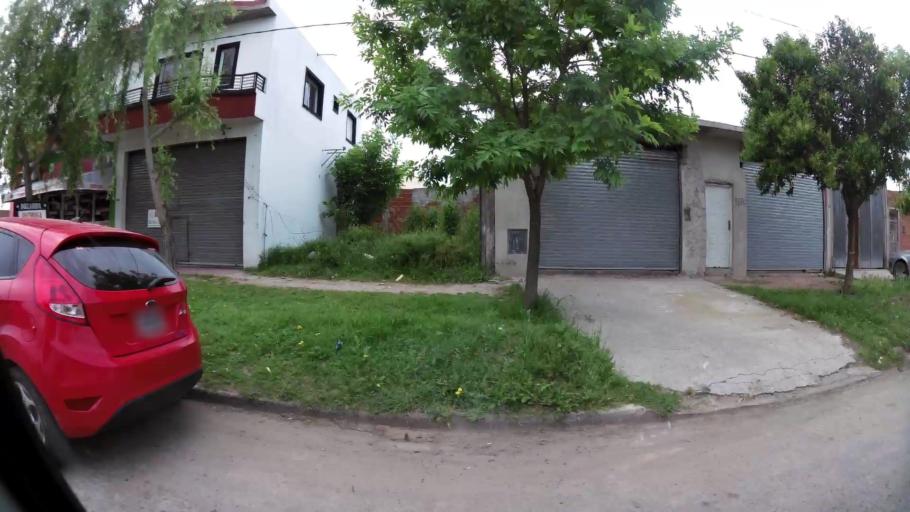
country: AR
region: Buenos Aires
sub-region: Partido de La Plata
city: La Plata
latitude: -34.9153
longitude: -57.9975
